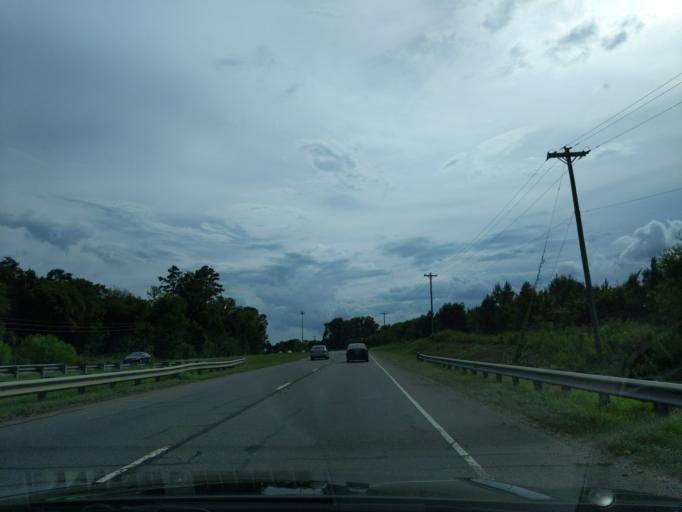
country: US
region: North Carolina
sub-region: Cabarrus County
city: Harrisburg
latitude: 35.3325
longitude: -80.6284
